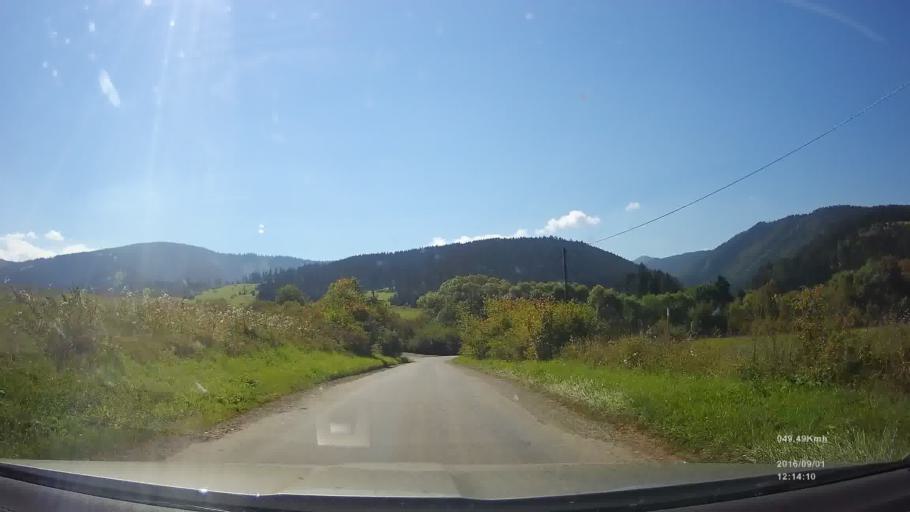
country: SK
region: Zilinsky
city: Ruzomberok
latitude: 49.0486
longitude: 19.4296
